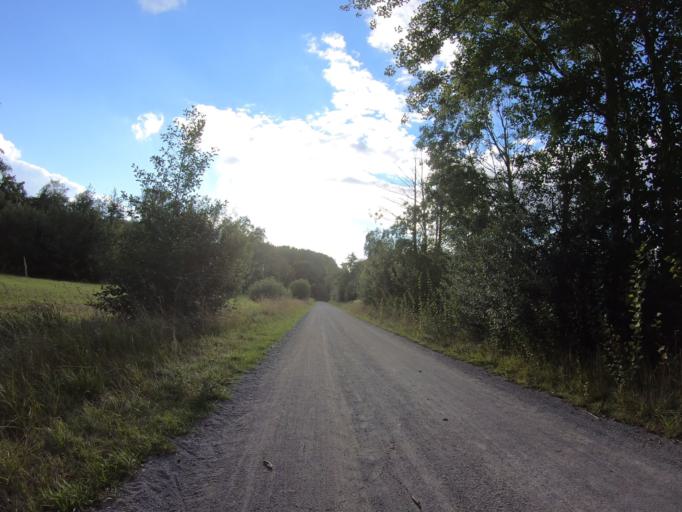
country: DE
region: Lower Saxony
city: Osloss
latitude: 52.4258
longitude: 10.6694
